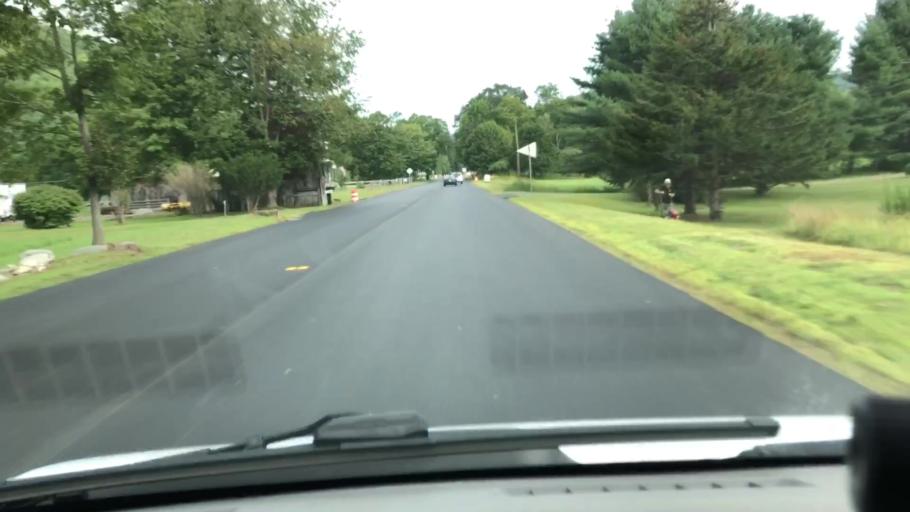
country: US
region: Massachusetts
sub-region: Franklin County
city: Charlemont
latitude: 42.6339
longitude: -72.9016
